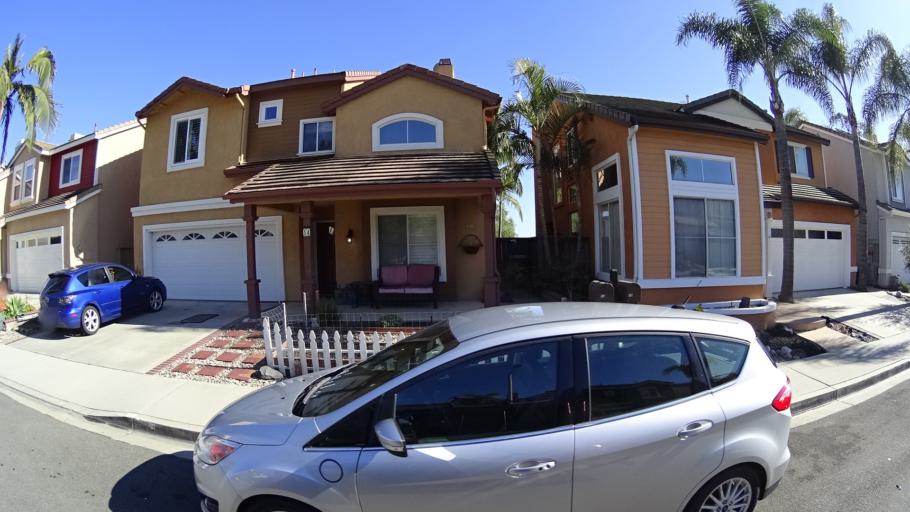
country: US
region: California
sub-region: Orange County
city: Aliso Viejo
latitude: 33.5776
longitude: -117.7363
